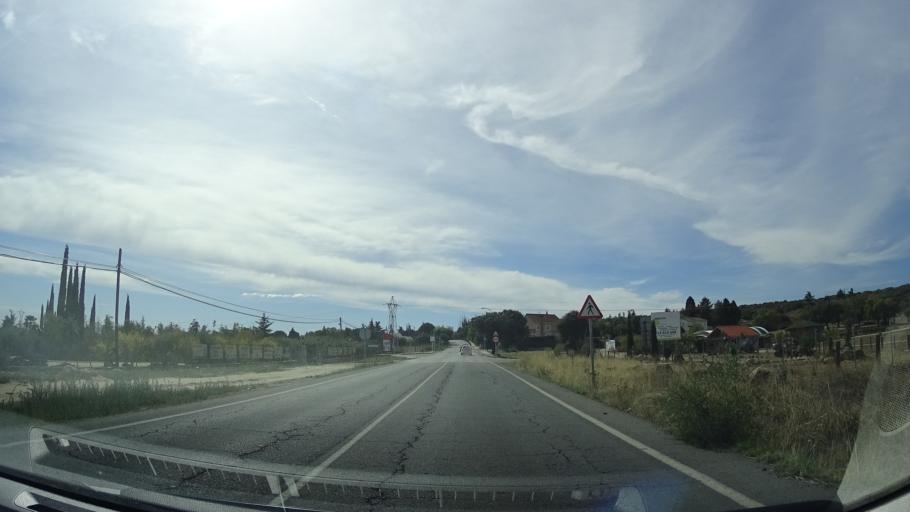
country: ES
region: Madrid
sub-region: Provincia de Madrid
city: Galapagar
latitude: 40.5897
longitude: -4.0116
